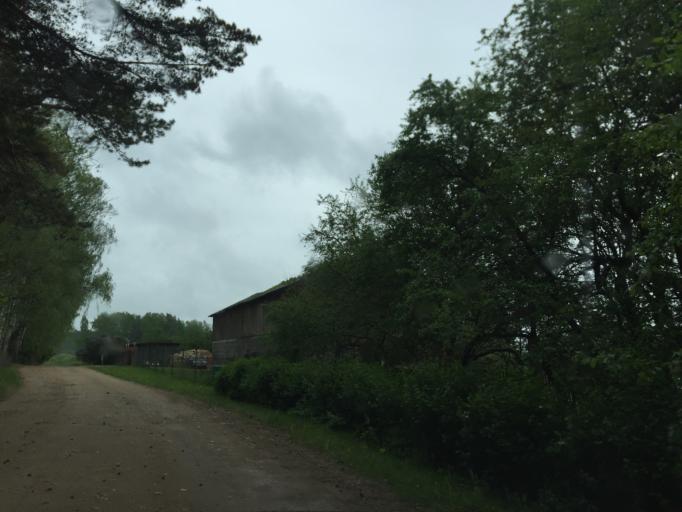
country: LV
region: Kegums
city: Kegums
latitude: 56.7359
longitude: 24.7417
